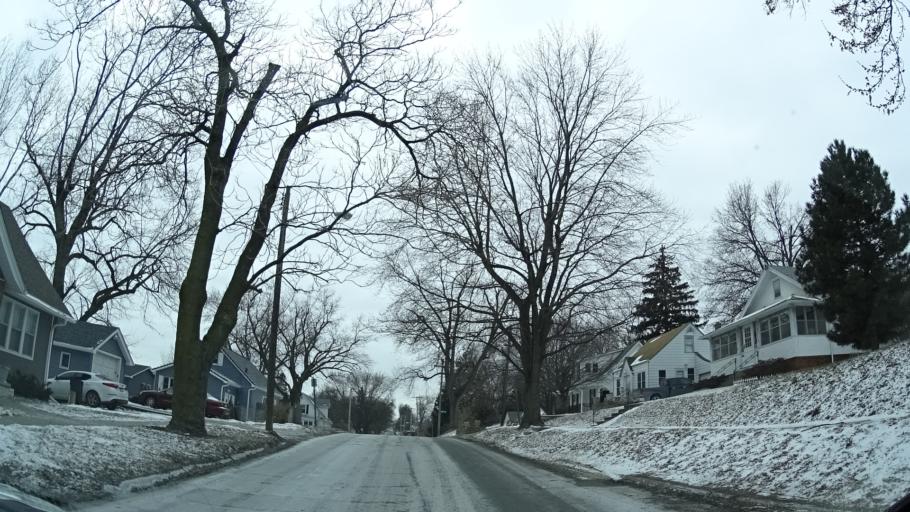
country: US
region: Nebraska
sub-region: Douglas County
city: Omaha
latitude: 41.2802
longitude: -96.0048
